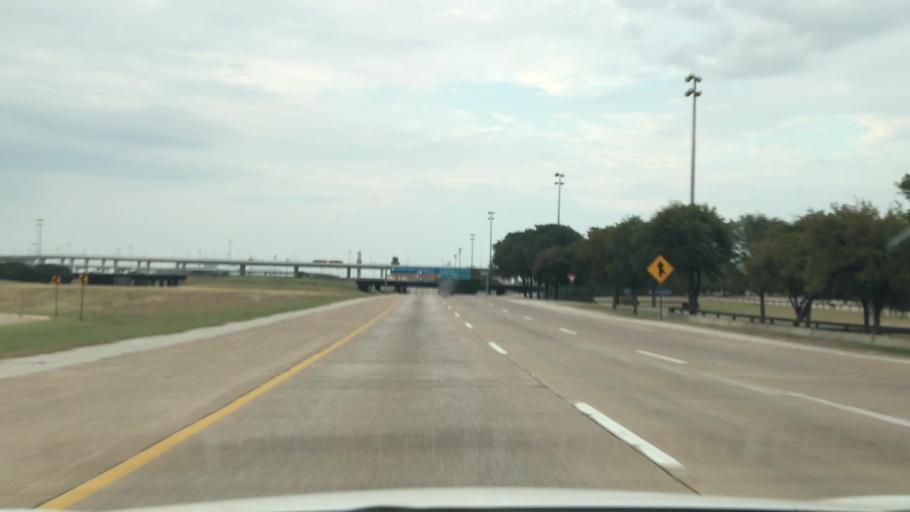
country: US
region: Texas
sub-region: Tarrant County
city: Euless
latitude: 32.8818
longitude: -97.0399
